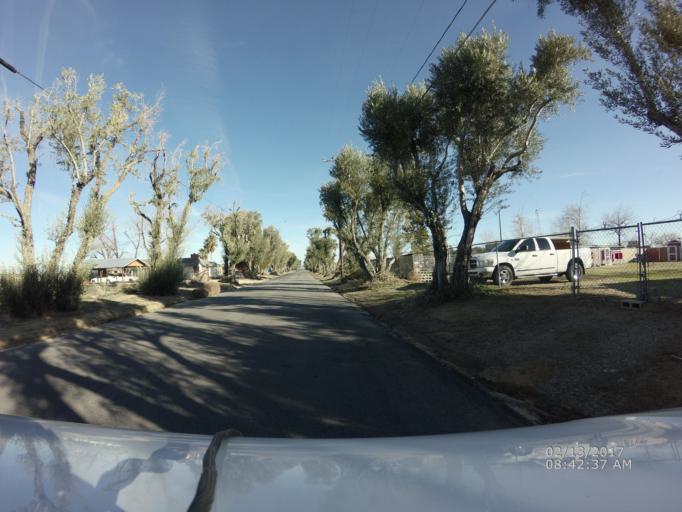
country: US
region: California
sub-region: Los Angeles County
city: Littlerock
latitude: 34.5290
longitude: -117.9881
